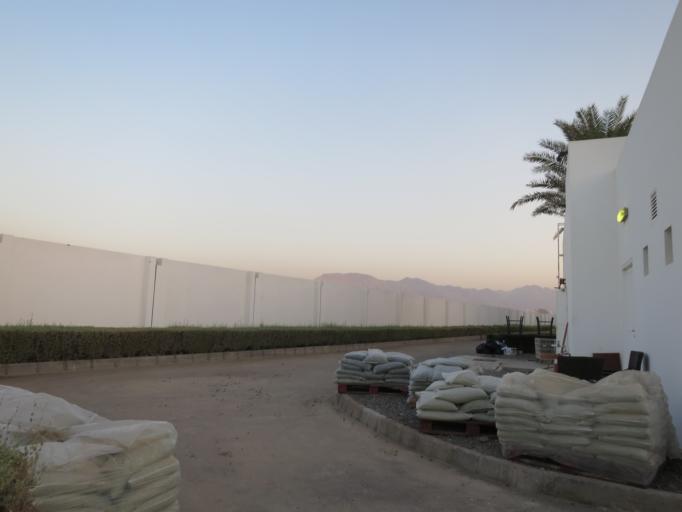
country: OM
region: Muhafazat Masqat
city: Bawshar
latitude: 23.6037
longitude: 58.4003
